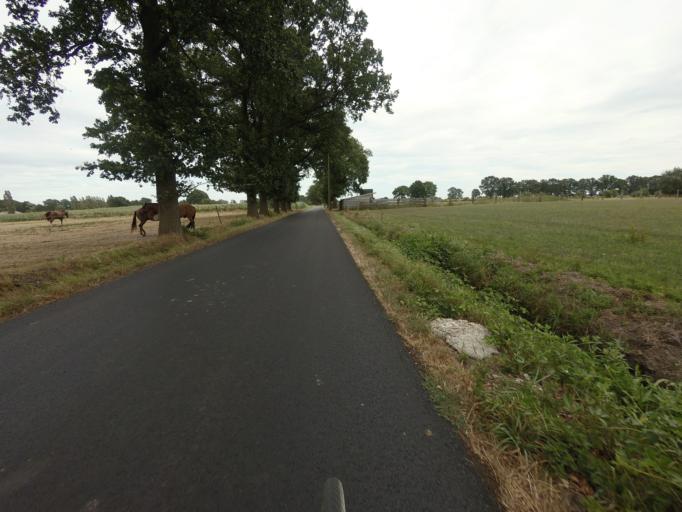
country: BE
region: Flanders
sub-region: Provincie Antwerpen
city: Brecht
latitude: 51.3244
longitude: 4.6448
